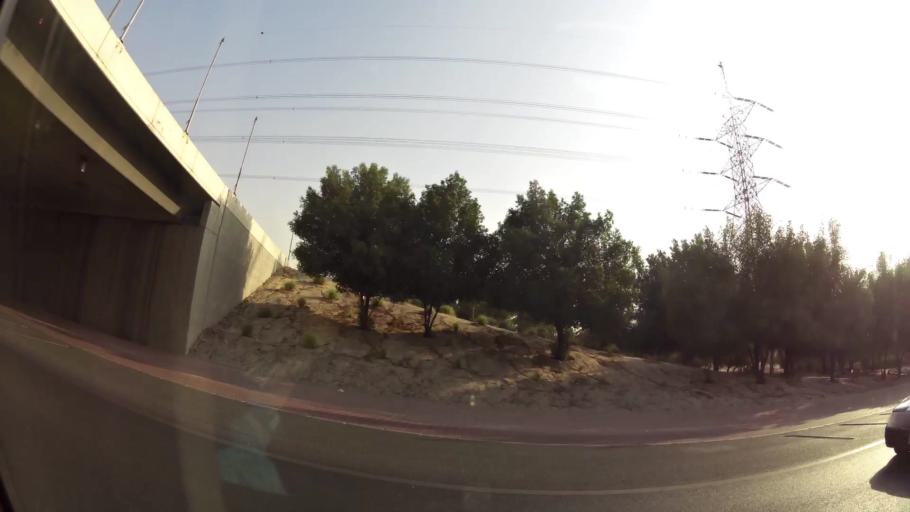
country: KW
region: Al Farwaniyah
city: Al Farwaniyah
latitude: 29.3038
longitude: 47.9789
